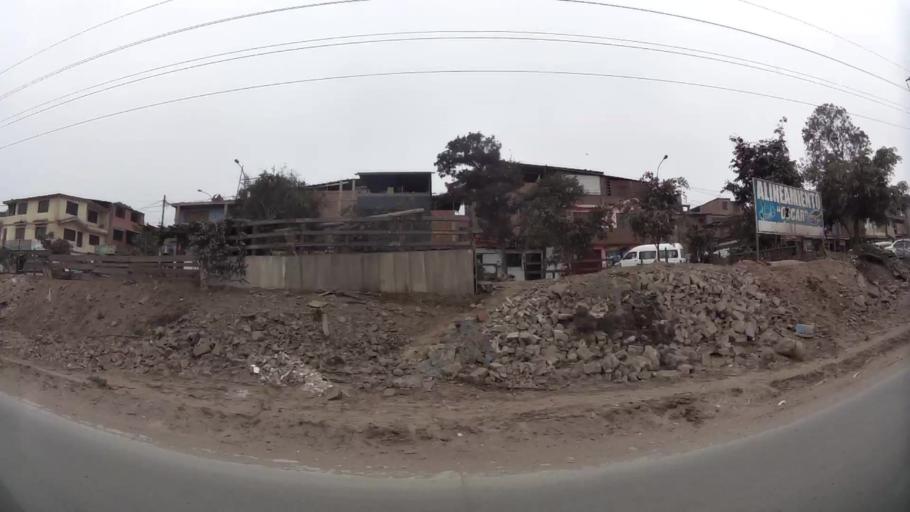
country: PE
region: Lima
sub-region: Lima
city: Surco
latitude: -12.1888
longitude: -76.9396
